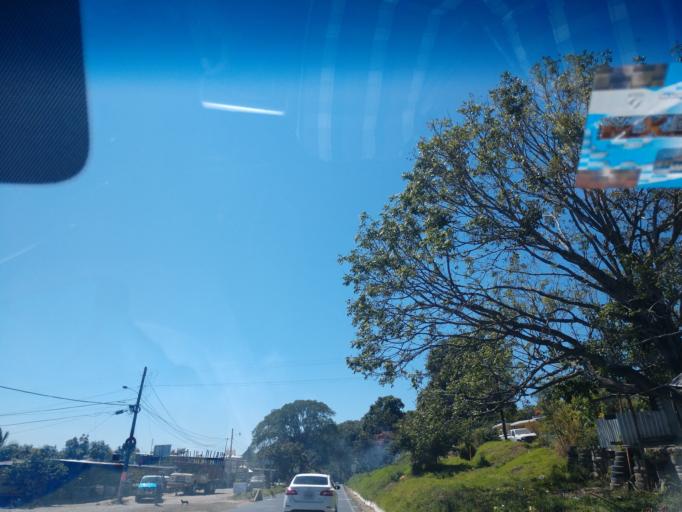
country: MX
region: Nayarit
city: Xalisco
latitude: 21.3999
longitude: -104.8951
